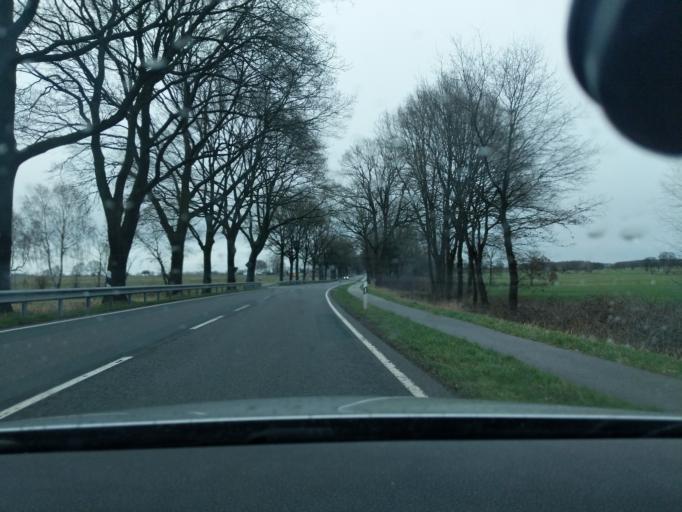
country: DE
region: Lower Saxony
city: Estorf
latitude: 53.5254
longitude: 9.2170
